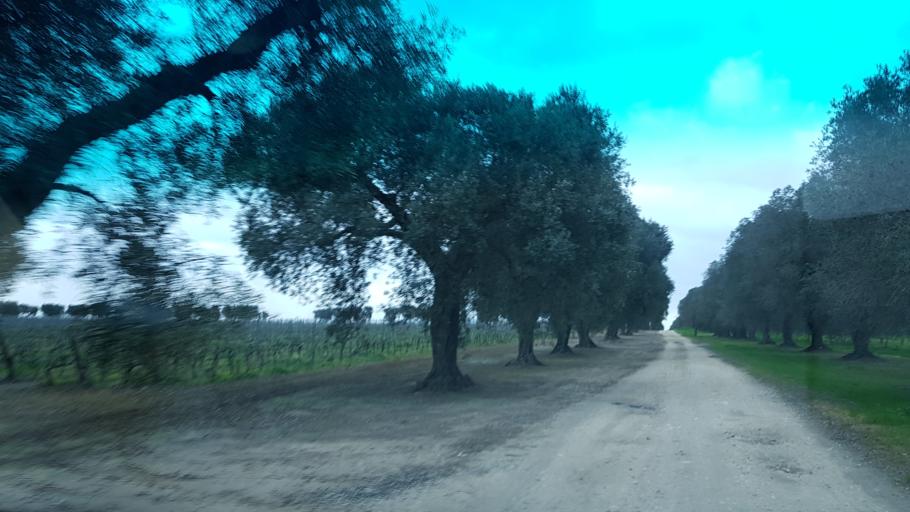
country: IT
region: Apulia
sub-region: Provincia di Brindisi
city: La Rosa
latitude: 40.5877
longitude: 17.9849
